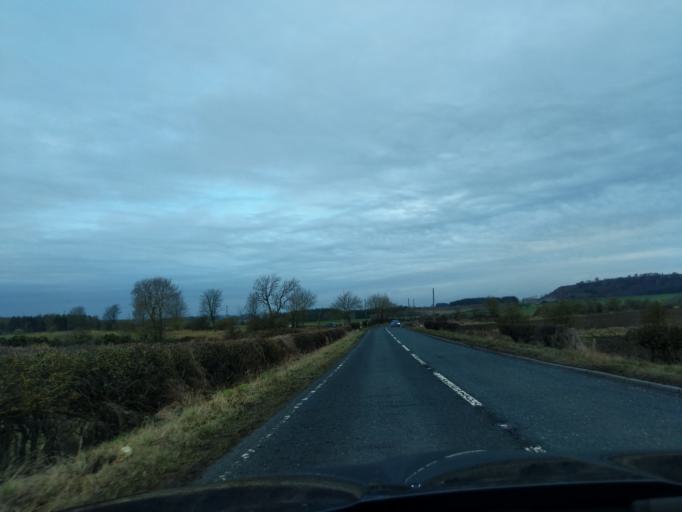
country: GB
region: England
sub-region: Northumberland
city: Rothley
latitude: 55.1186
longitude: -1.9075
